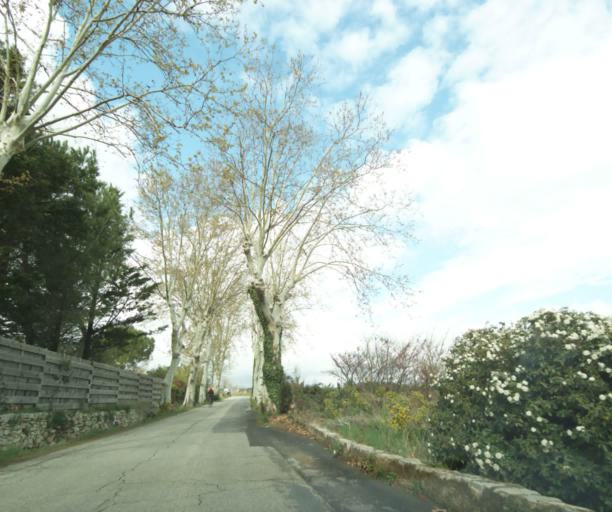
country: FR
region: Languedoc-Roussillon
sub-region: Departement de l'Herault
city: Cournonterral
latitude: 43.5626
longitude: 3.7292
